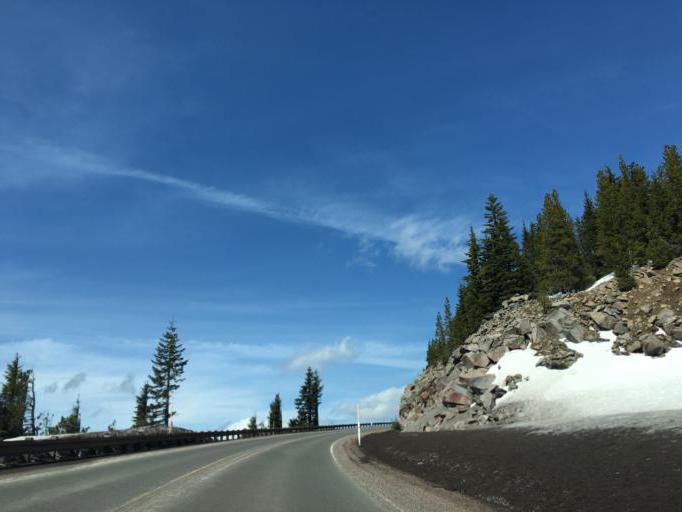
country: US
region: Oregon
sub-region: Clackamas County
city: Mount Hood Village
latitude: 45.3079
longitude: -121.7059
